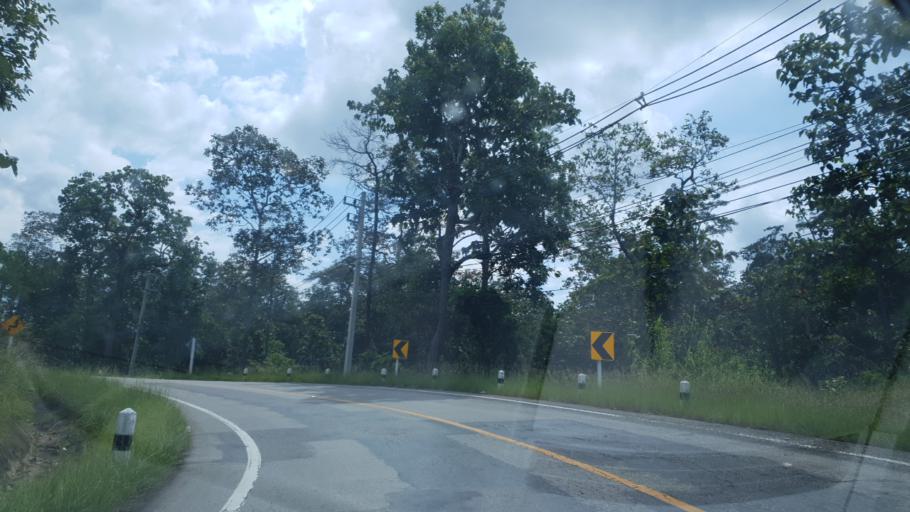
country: TH
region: Mae Hong Son
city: Khun Yuam
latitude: 18.7749
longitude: 97.9404
